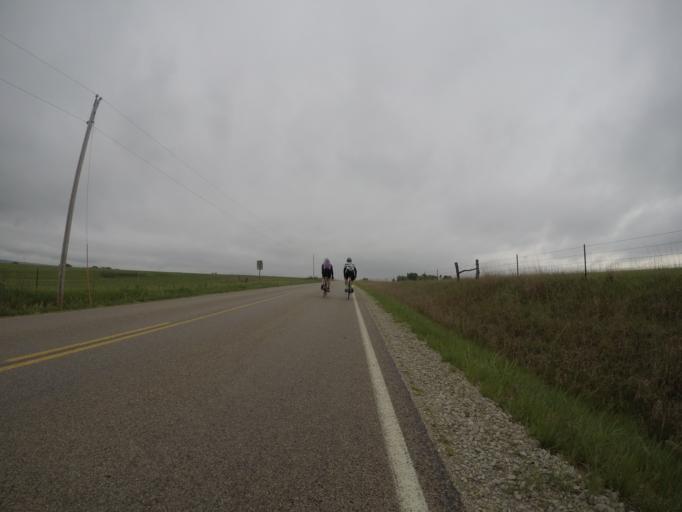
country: US
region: Kansas
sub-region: Pottawatomie County
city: Westmoreland
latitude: 39.4620
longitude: -96.1839
